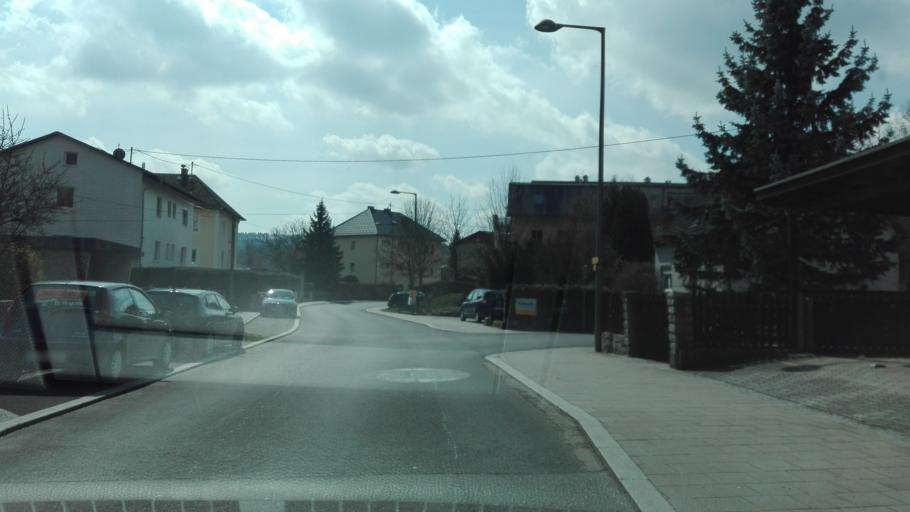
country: AT
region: Upper Austria
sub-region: Politischer Bezirk Urfahr-Umgebung
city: Ottensheim
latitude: 48.3354
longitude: 14.1811
